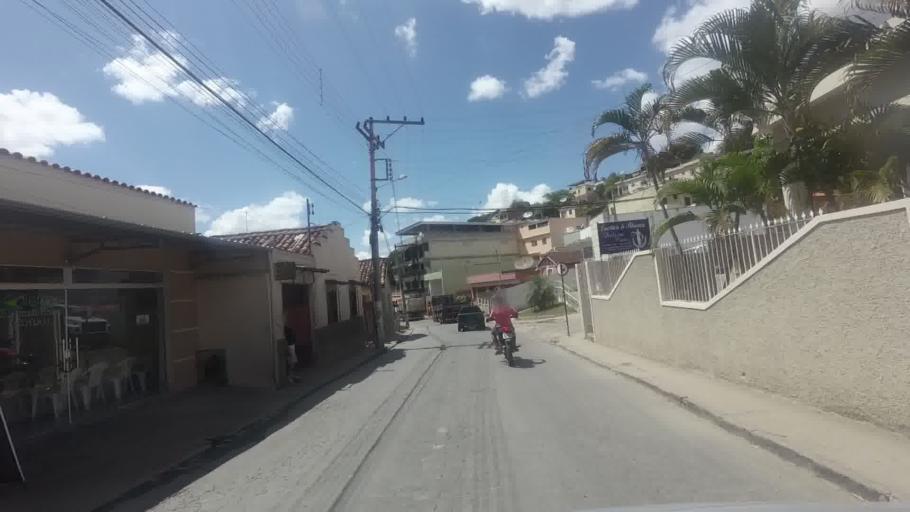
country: BR
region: Minas Gerais
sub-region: Recreio
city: Recreio
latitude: -21.6588
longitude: -42.3475
